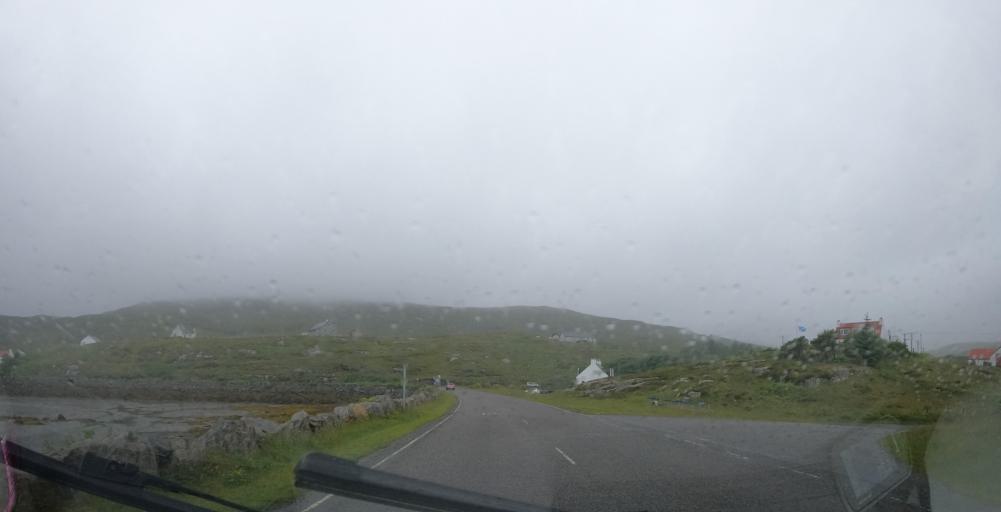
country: GB
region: Scotland
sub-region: Eilean Siar
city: Barra
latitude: 57.0027
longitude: -7.4295
